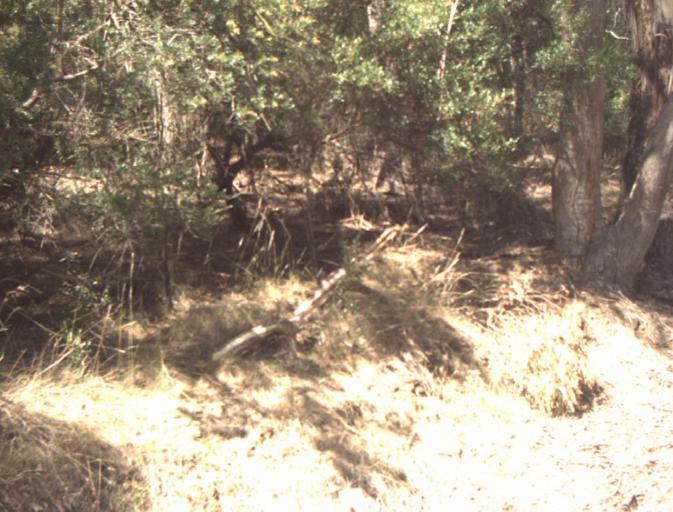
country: AU
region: Tasmania
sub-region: Launceston
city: Summerhill
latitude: -41.4576
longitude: 147.1189
